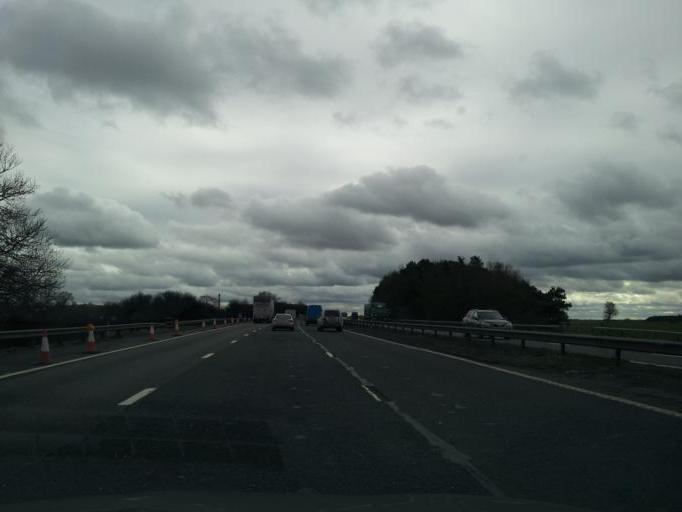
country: GB
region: England
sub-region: Staffordshire
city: Stone
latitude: 52.8811
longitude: -2.1662
